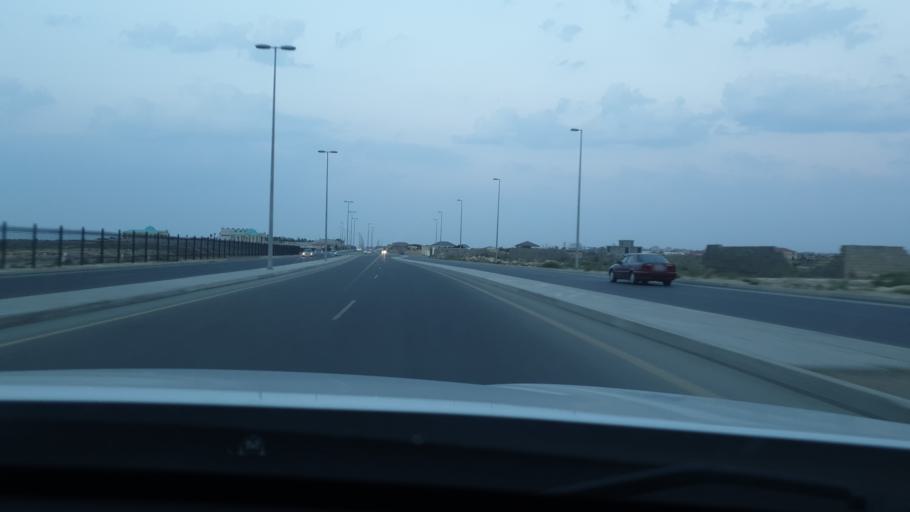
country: AZ
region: Baki
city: Nardaran
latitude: 40.5822
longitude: 50.0076
